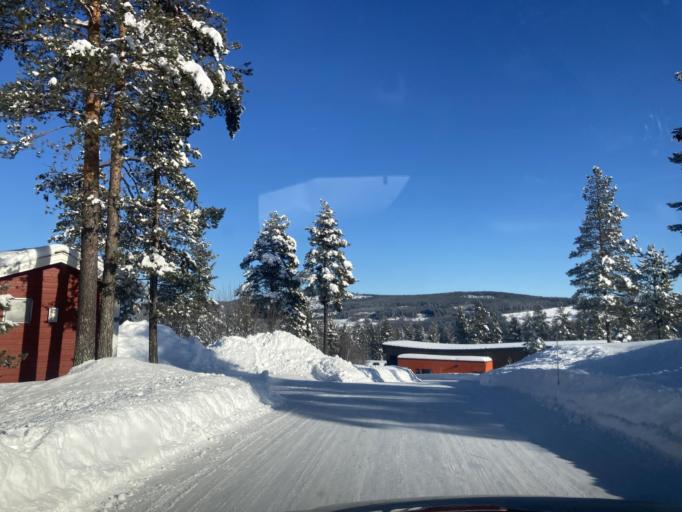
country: NO
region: Hedmark
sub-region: Trysil
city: Innbygda
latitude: 61.2992
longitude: 12.2428
